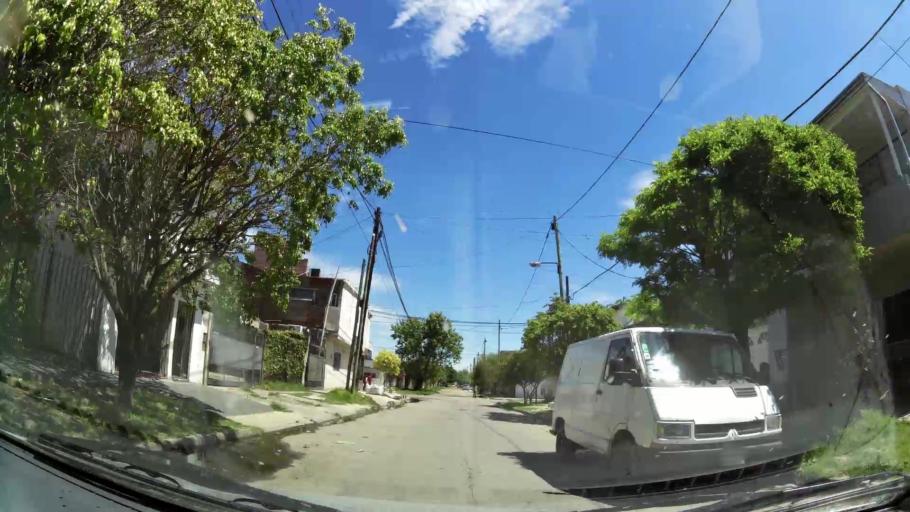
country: AR
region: Buenos Aires
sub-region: Partido de Quilmes
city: Quilmes
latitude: -34.7282
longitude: -58.3094
